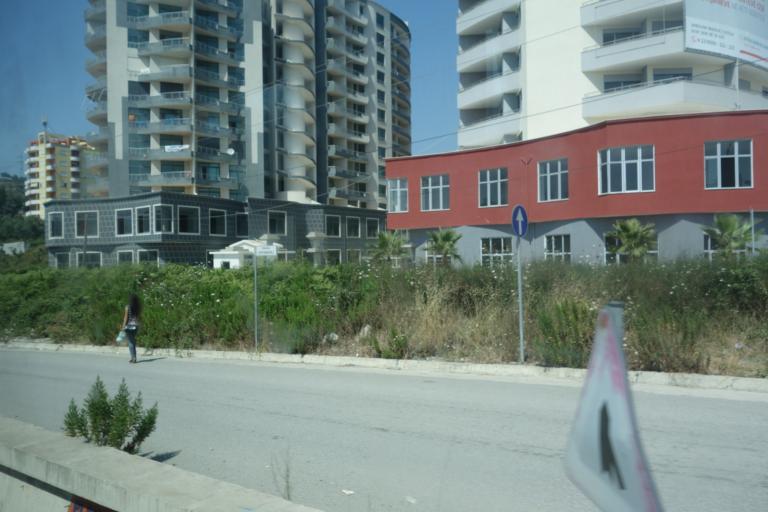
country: AL
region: Tirane
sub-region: Rrethi i Kavajes
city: Golem
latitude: 41.2673
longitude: 19.5219
